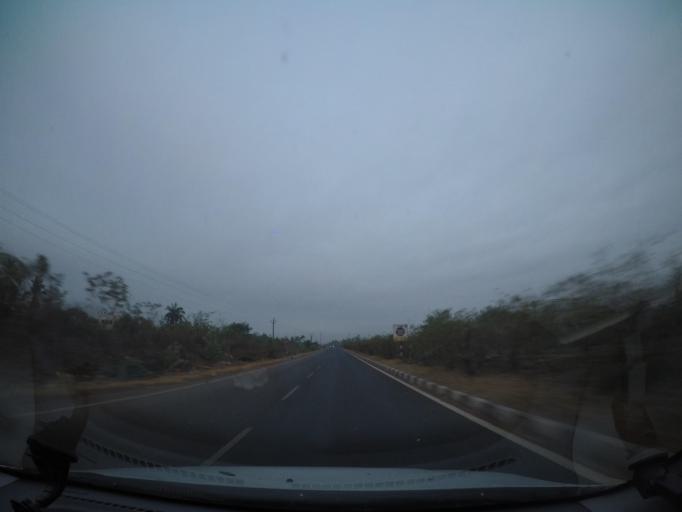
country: IN
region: Andhra Pradesh
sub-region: West Godavari
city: Tadepallegudem
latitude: 16.8090
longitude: 81.3215
